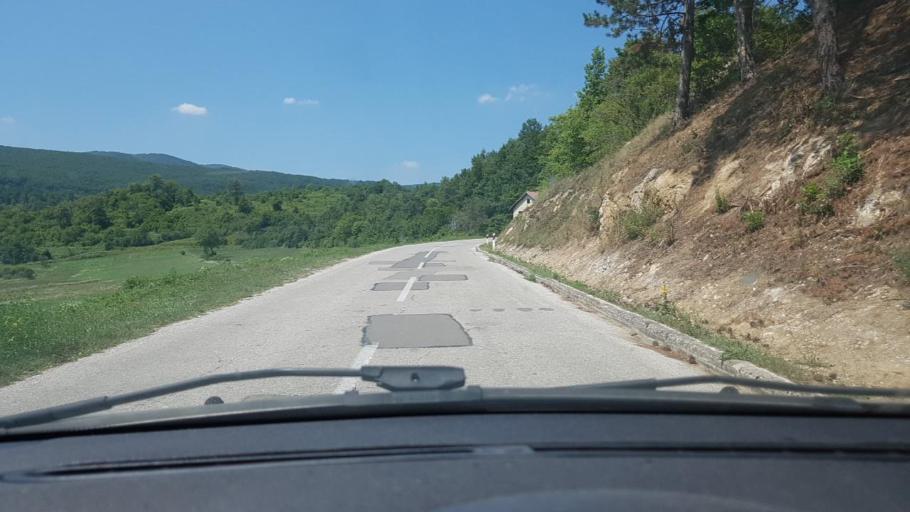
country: BA
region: Federation of Bosnia and Herzegovina
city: Orasac
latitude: 44.5947
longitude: 16.0778
